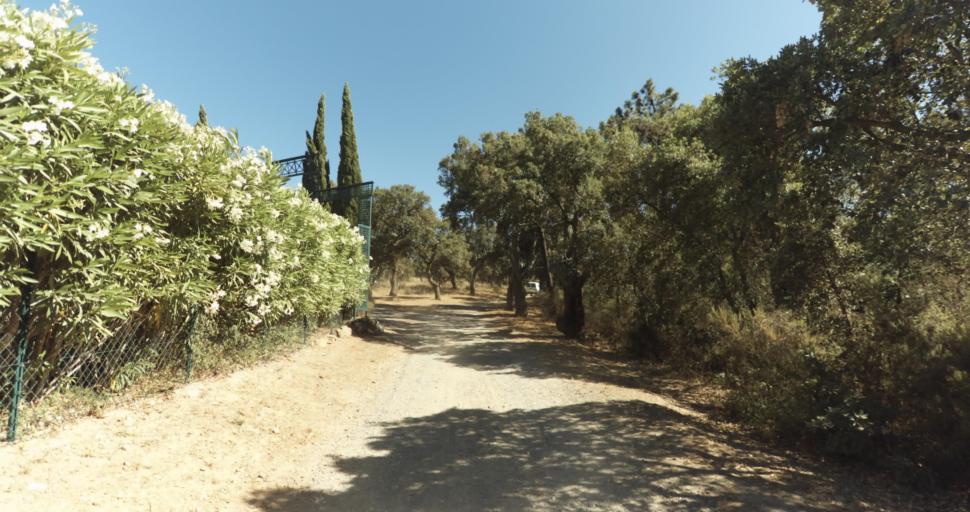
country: FR
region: Provence-Alpes-Cote d'Azur
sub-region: Departement du Var
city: Gassin
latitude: 43.2351
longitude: 6.5851
